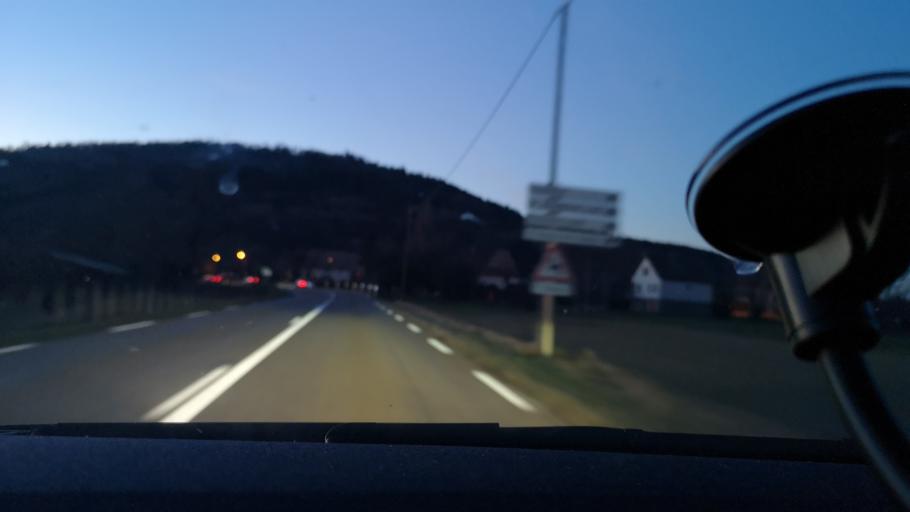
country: FR
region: Franche-Comte
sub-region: Departement du Jura
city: Champagnole
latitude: 46.7581
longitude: 5.9425
